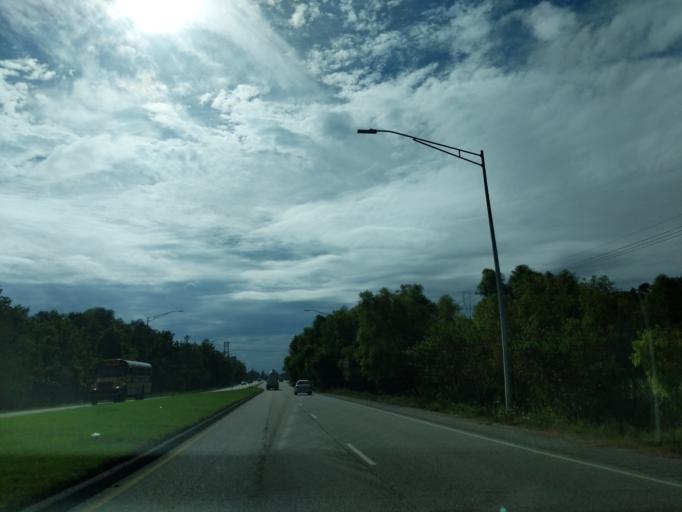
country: US
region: Louisiana
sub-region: Saint Bernard Parish
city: Chalmette
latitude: 30.0394
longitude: -89.9024
